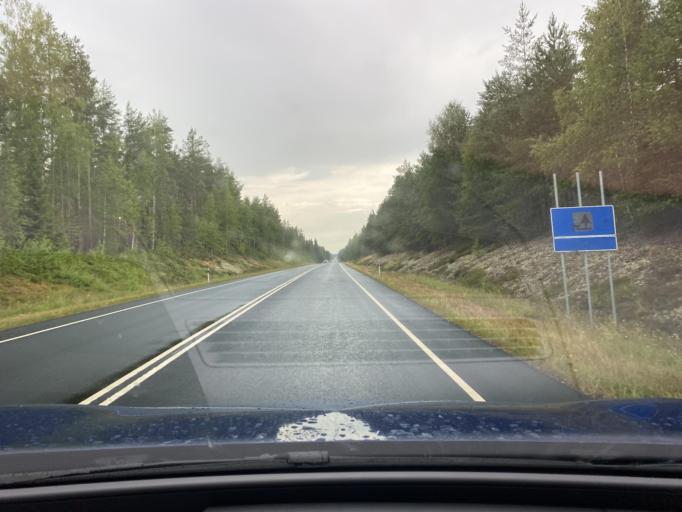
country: FI
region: Central Ostrobothnia
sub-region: Kaustinen
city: Veteli
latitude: 63.4129
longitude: 23.9532
